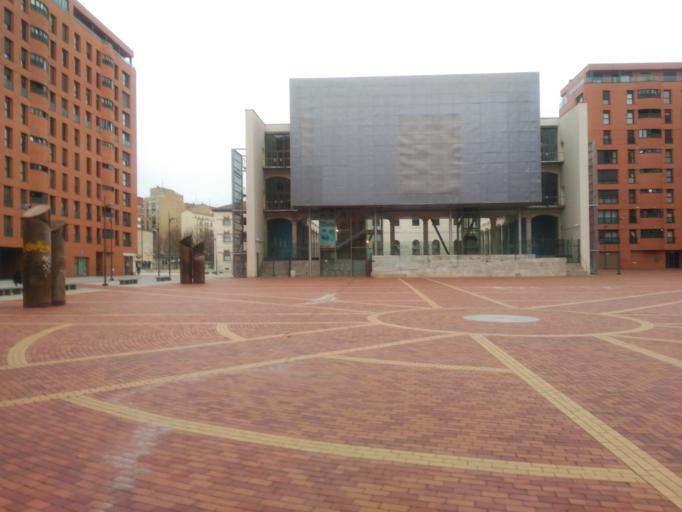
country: ES
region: Castille and Leon
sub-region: Provincia de Burgos
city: Burgos
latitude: 42.3341
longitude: -3.7015
